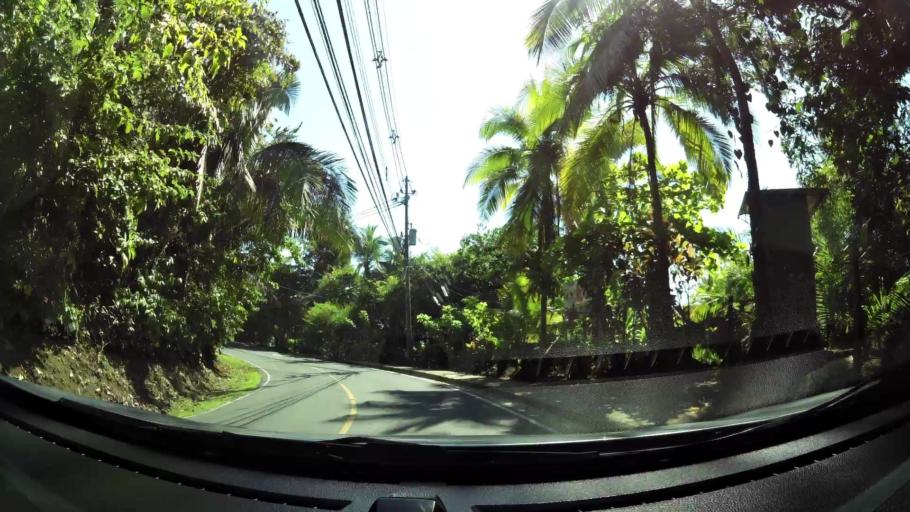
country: CR
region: Puntarenas
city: Quepos
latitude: 9.3924
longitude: -84.1505
